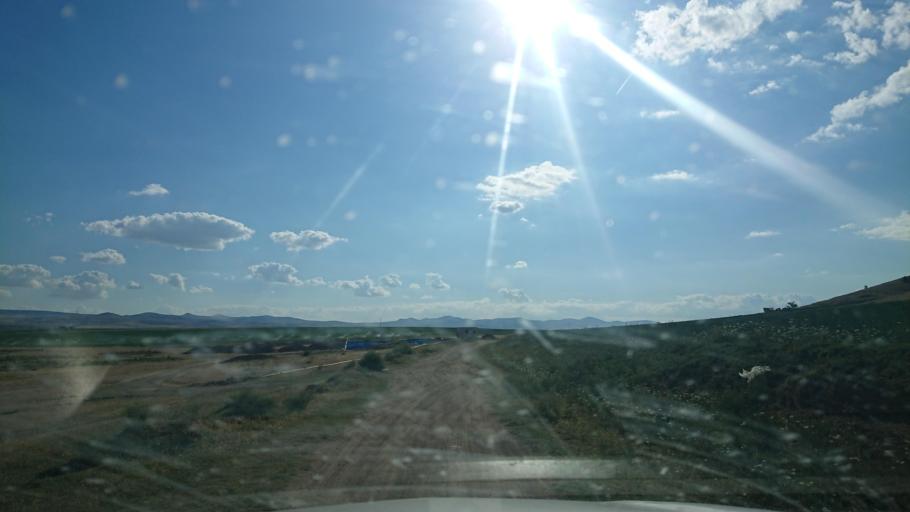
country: TR
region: Aksaray
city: Sariyahsi
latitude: 39.0192
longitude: 33.8951
